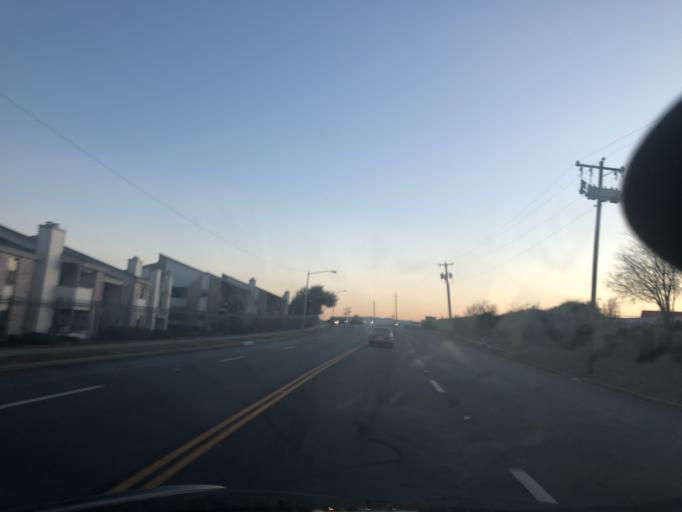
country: US
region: Texas
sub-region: Tarrant County
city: White Settlement
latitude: 32.7321
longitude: -97.4790
